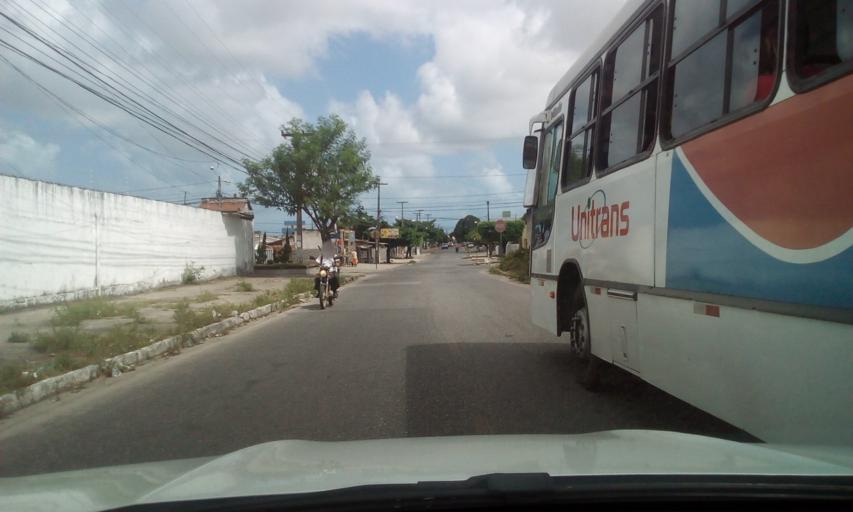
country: BR
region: Paraiba
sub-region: Joao Pessoa
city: Joao Pessoa
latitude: -7.1654
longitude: -34.8587
